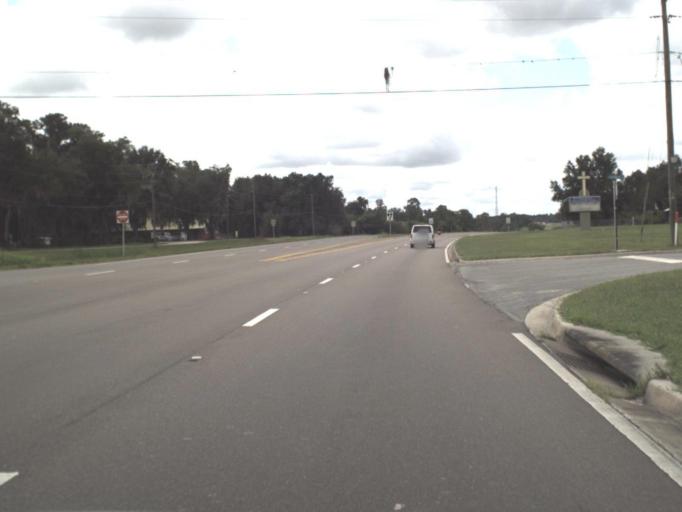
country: US
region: Florida
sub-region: Hardee County
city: Bowling Green
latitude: 27.6279
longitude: -81.8247
